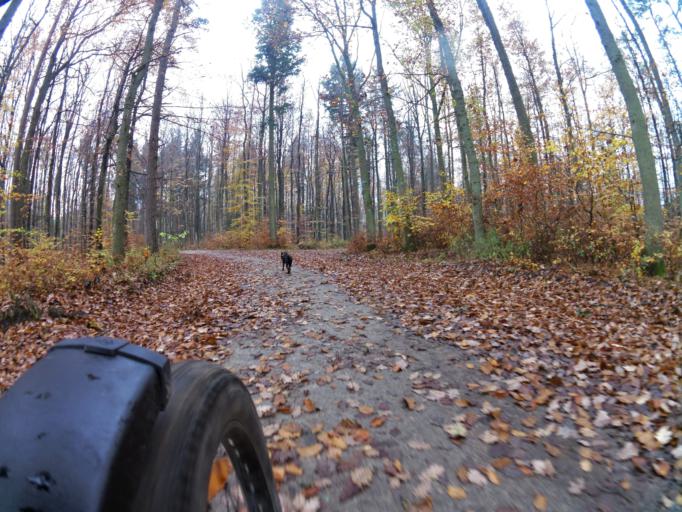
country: PL
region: Pomeranian Voivodeship
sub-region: Powiat pucki
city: Krokowa
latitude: 54.7669
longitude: 18.0949
